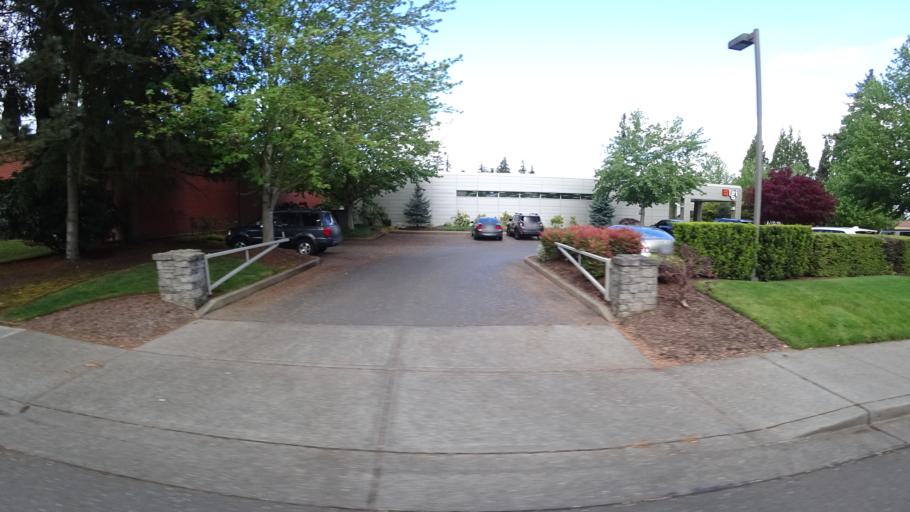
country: US
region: Oregon
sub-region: Washington County
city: Durham
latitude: 45.3985
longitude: -122.7439
